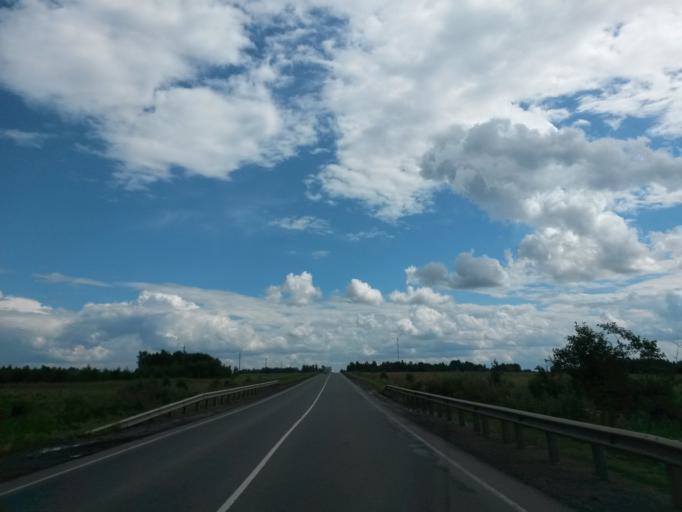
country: RU
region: Jaroslavl
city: Dubki
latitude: 57.2152
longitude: 40.2820
